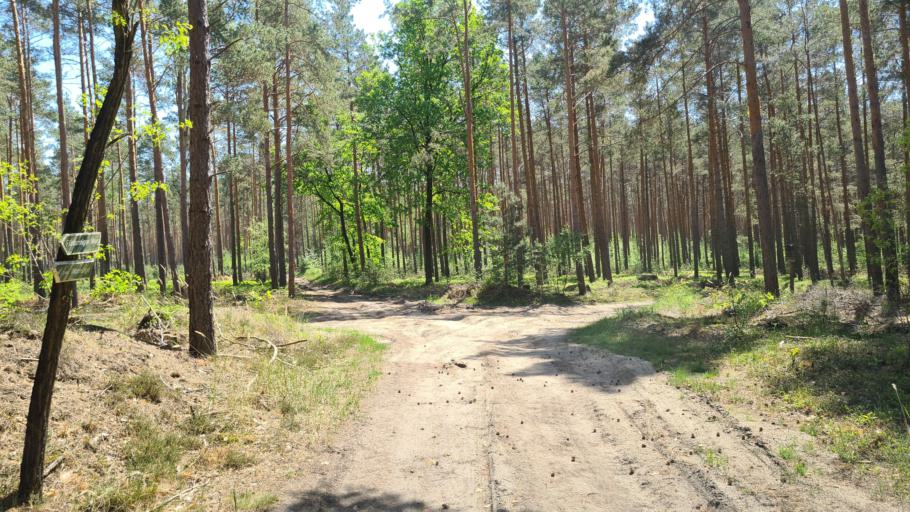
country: DE
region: Brandenburg
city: Sallgast
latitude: 51.5855
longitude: 13.8772
